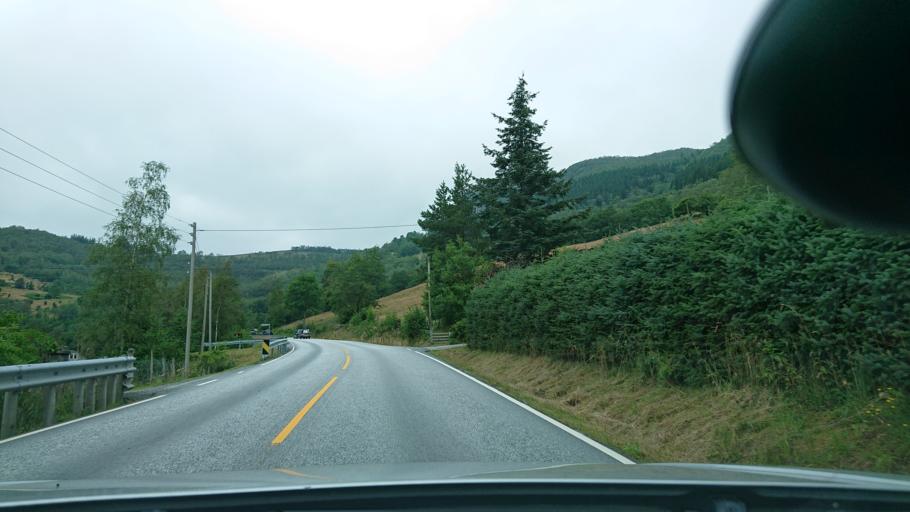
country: NO
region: Rogaland
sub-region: Hjelmeland
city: Hjelmelandsvagen
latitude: 59.1695
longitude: 6.1690
